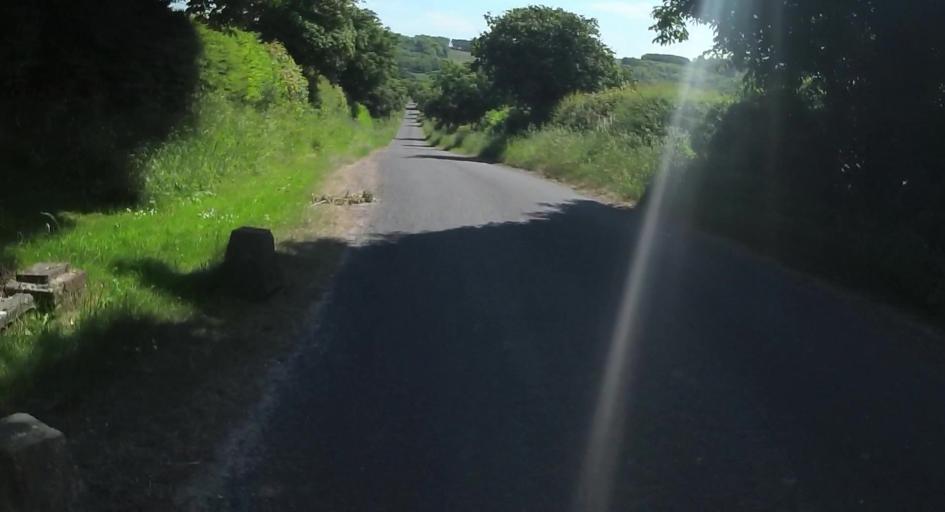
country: GB
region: England
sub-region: Hampshire
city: Kingsclere
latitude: 51.3188
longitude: -1.2952
